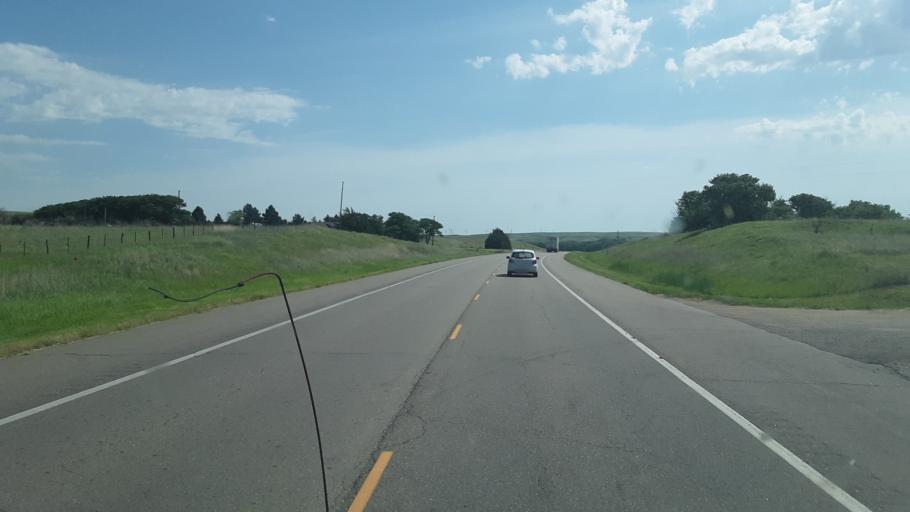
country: US
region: Kansas
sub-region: Ellsworth County
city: Ellsworth
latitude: 38.8340
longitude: -98.1240
